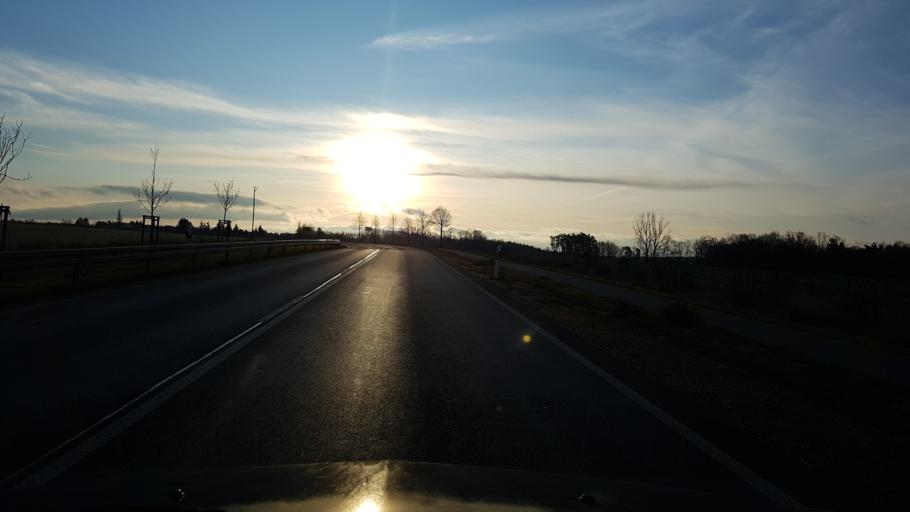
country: DE
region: Saxony
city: Radibor
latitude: 51.2312
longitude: 14.3770
